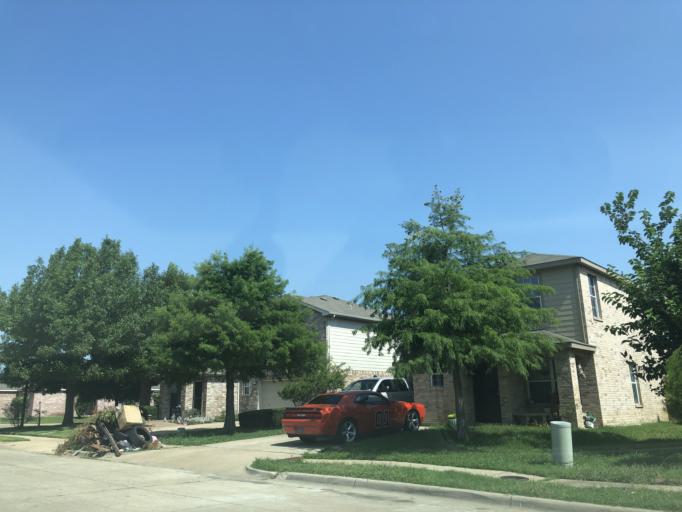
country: US
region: Texas
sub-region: Dallas County
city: Dallas
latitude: 32.7908
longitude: -96.8630
